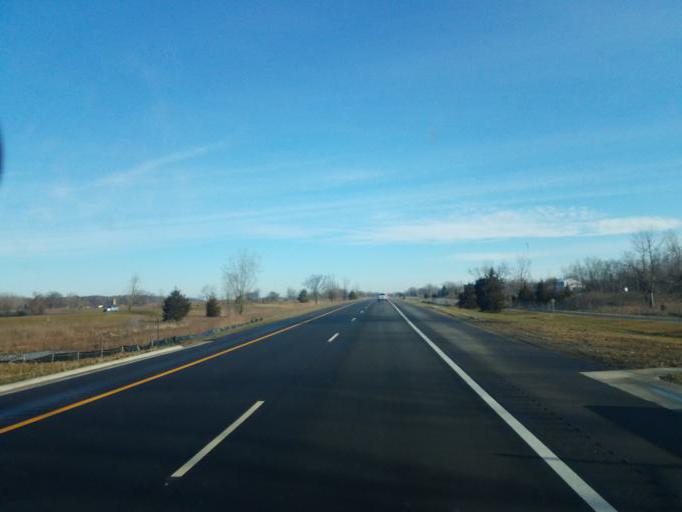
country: US
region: Michigan
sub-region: Gratiot County
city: Ithaca
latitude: 43.3355
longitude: -84.6013
